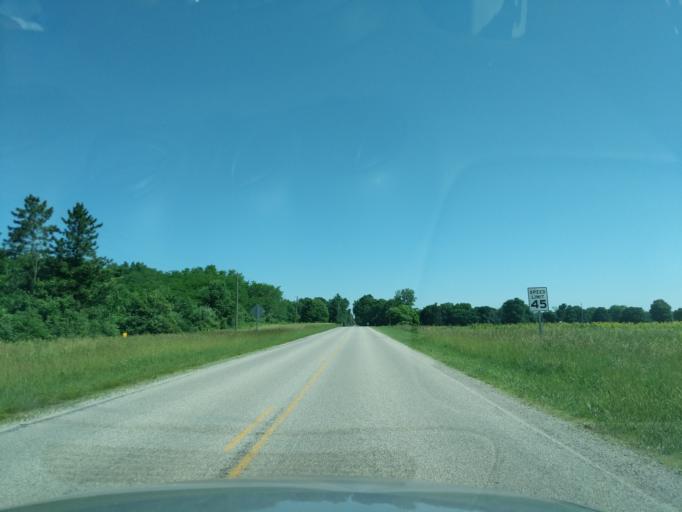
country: US
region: Indiana
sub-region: Huntington County
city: Warren
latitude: 40.7436
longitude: -85.5070
